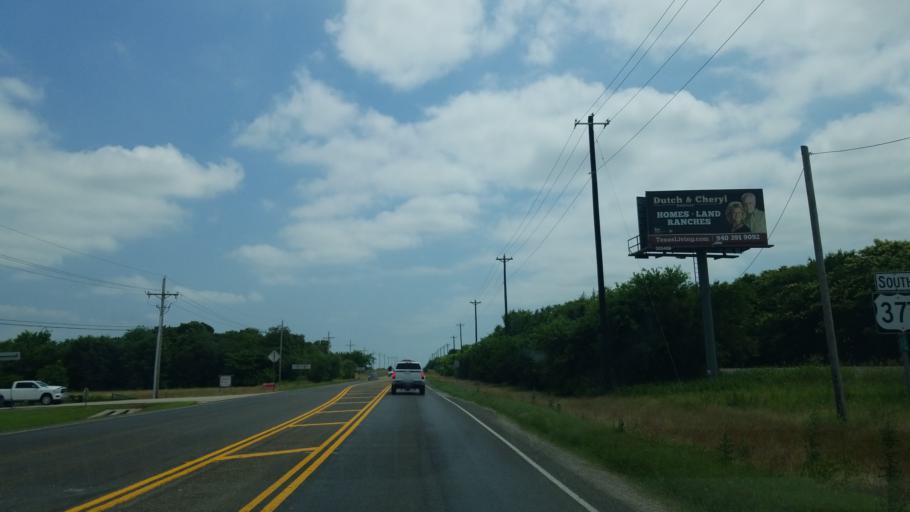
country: US
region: Texas
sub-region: Denton County
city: Pilot Point
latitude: 33.3676
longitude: -96.9645
